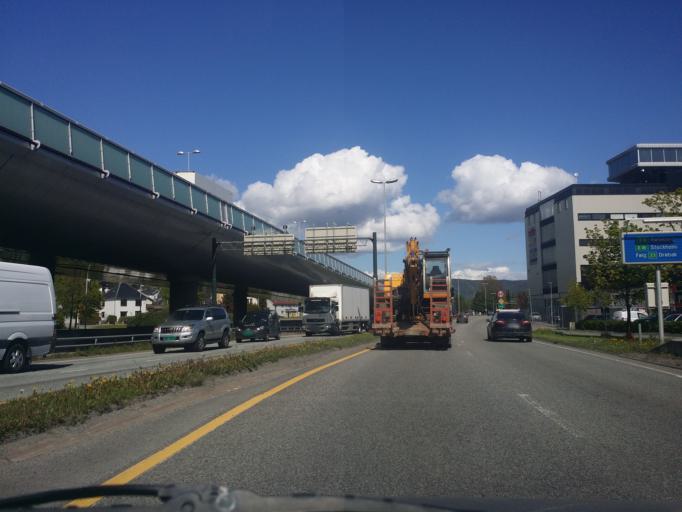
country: NO
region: Buskerud
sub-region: Drammen
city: Drammen
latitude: 59.7426
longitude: 10.2290
